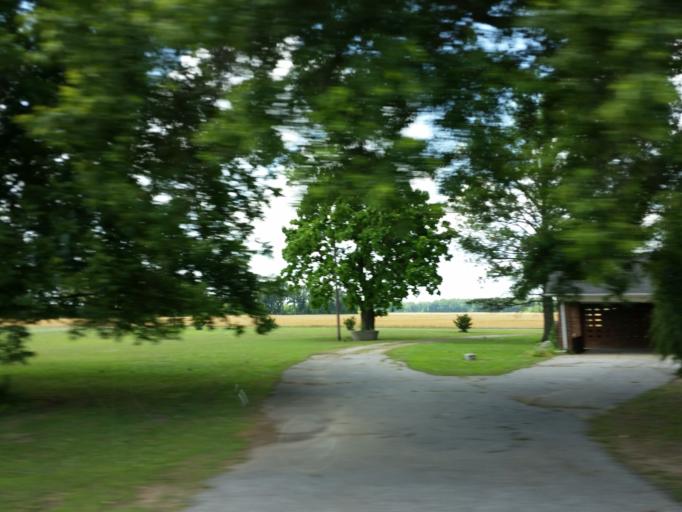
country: US
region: Tennessee
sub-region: Lake County
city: Ridgely
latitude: 36.1839
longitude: -89.4492
